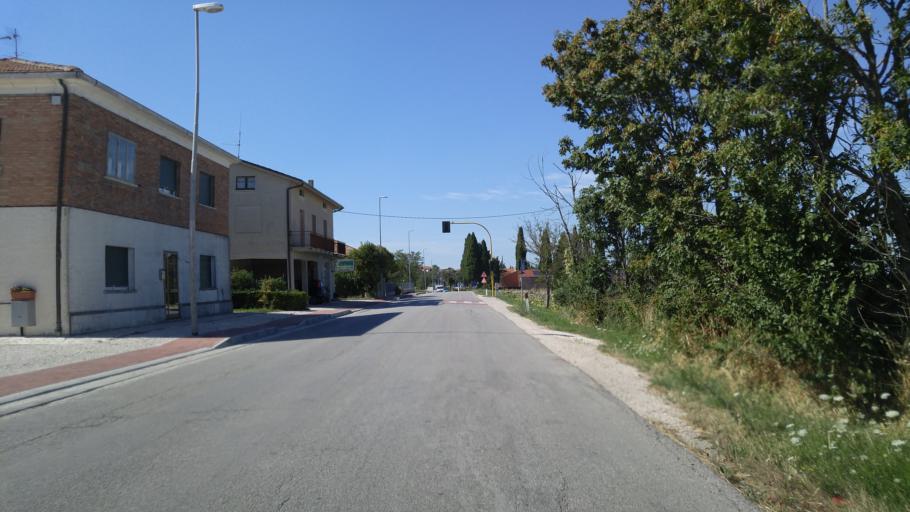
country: IT
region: The Marches
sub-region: Provincia di Pesaro e Urbino
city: San Giorgio di Pesaro
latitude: 43.7134
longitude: 12.9857
